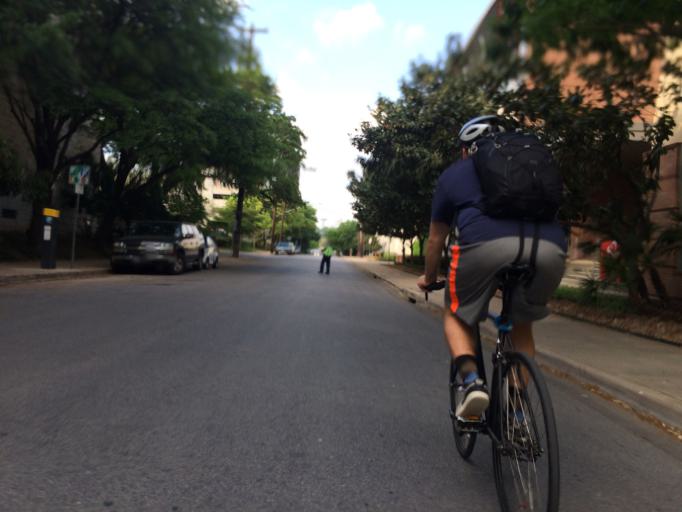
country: US
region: Texas
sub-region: Travis County
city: Austin
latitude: 30.2716
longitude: -97.7527
